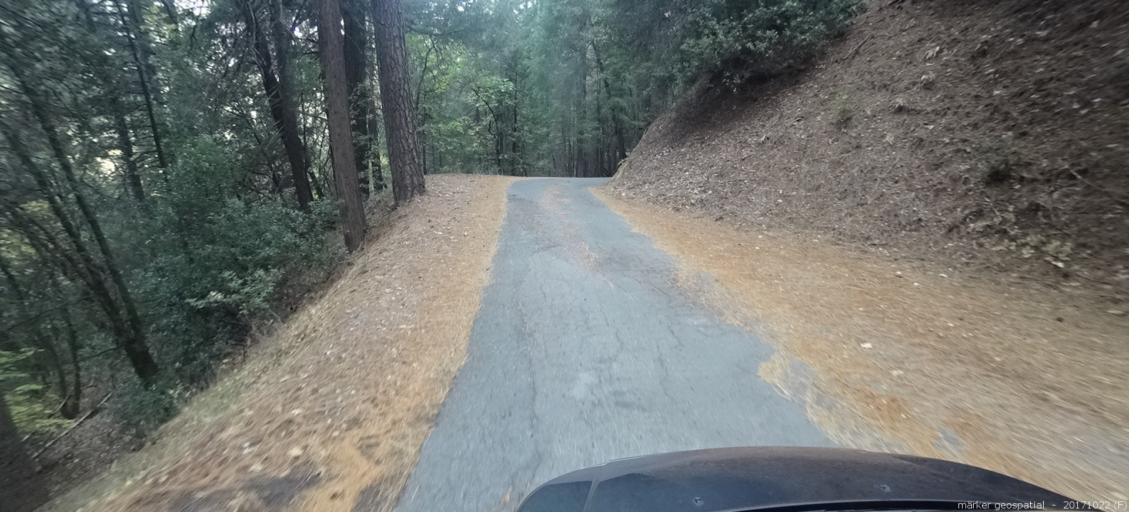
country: US
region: California
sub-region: Siskiyou County
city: Dunsmuir
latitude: 41.1584
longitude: -122.2881
